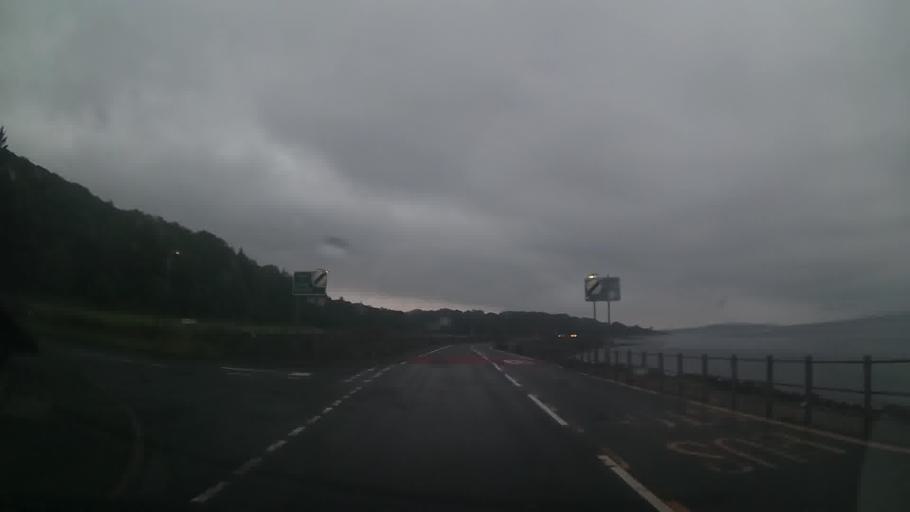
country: GB
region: Scotland
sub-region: North Ayrshire
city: Skelmorlie
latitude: 55.8552
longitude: -4.8895
